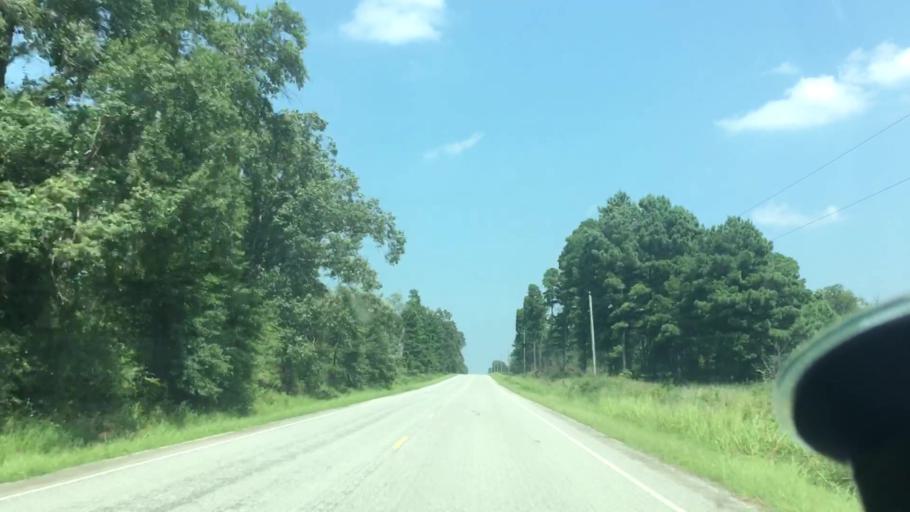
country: US
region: Oklahoma
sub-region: Atoka County
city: Atoka
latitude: 34.2610
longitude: -95.9361
